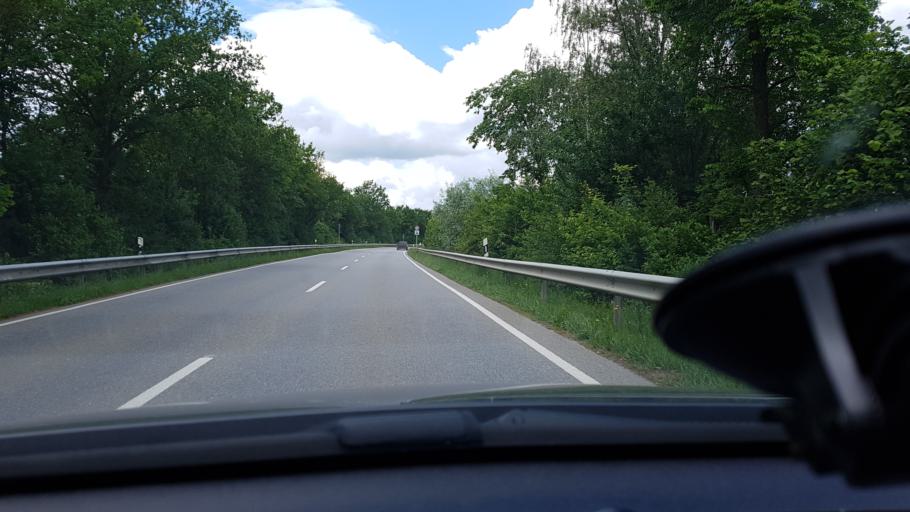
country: DE
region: Bavaria
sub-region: Lower Bavaria
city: Kirchham
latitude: 48.3529
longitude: 13.2380
